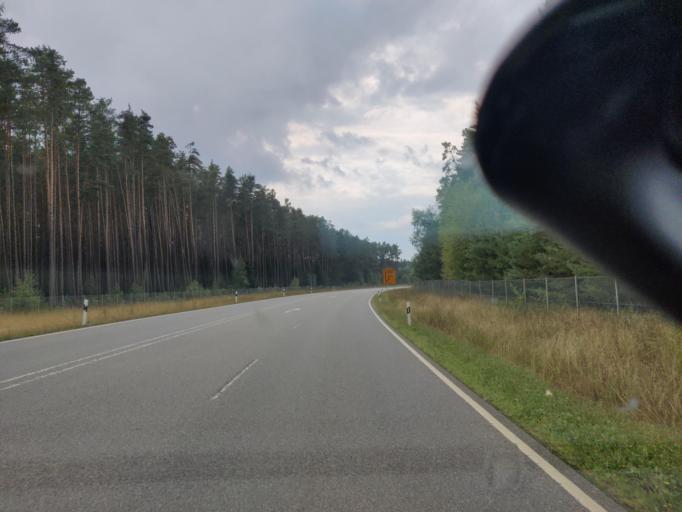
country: DE
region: Bavaria
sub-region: Regierungsbezirk Mittelfranken
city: Rottenbach
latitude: 49.1473
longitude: 11.0414
